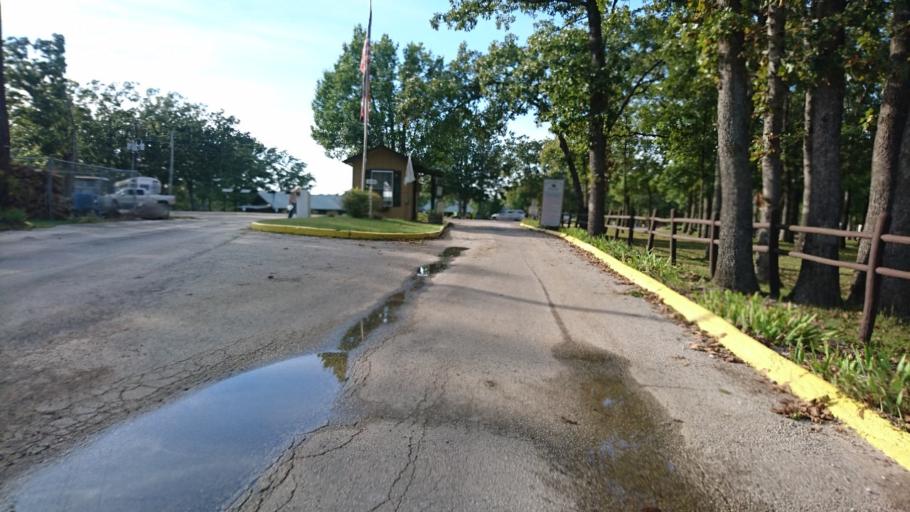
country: US
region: Missouri
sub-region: Crawford County
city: Cuba
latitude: 38.1106
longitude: -91.3591
